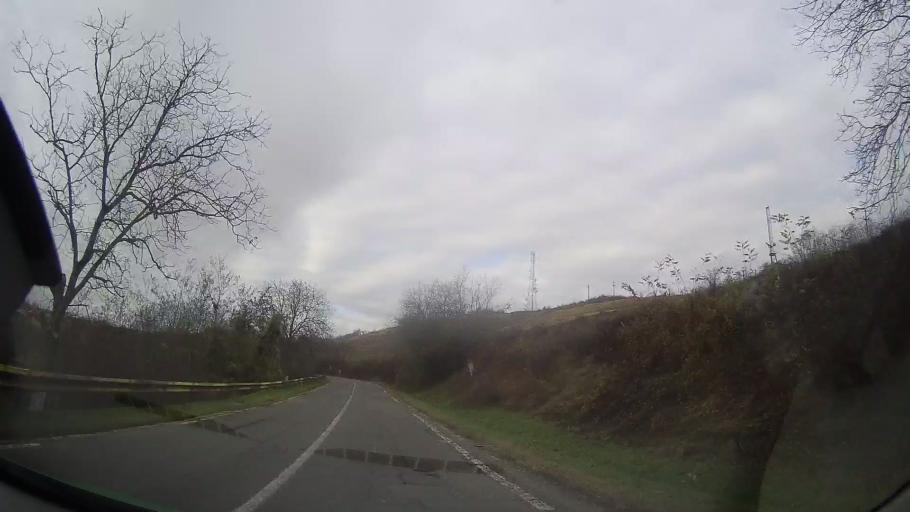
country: RO
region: Bistrita-Nasaud
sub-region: Comuna Silvasu de Campie
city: Silvasu de Campie
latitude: 46.7769
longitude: 24.3225
